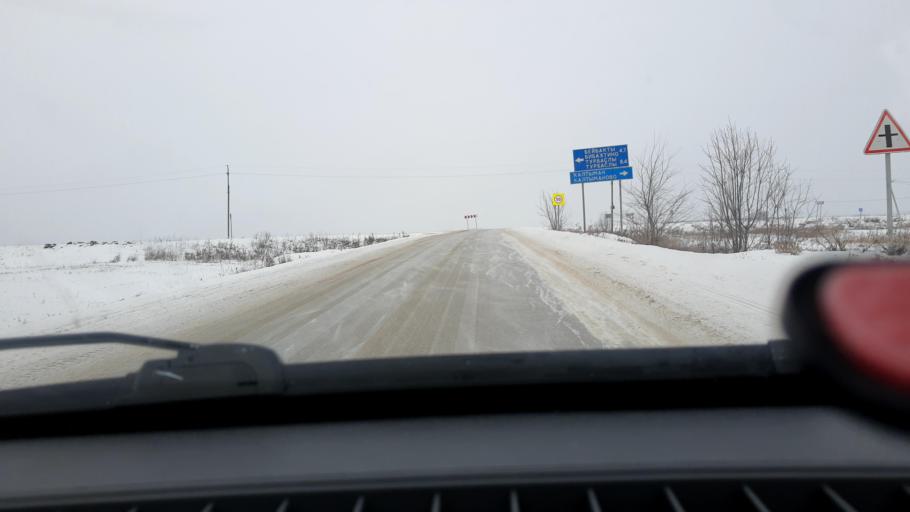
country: RU
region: Bashkortostan
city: Iglino
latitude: 54.7076
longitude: 56.4012
